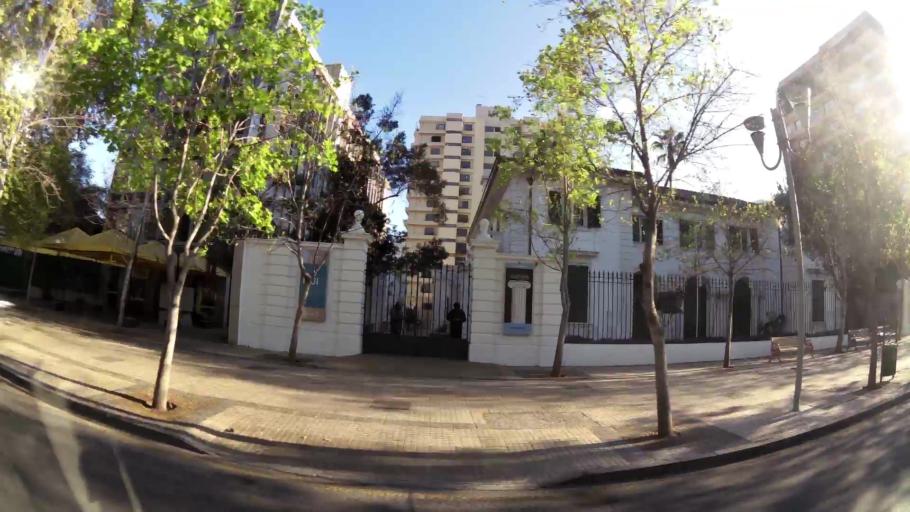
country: CL
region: Santiago Metropolitan
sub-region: Provincia de Santiago
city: Villa Presidente Frei, Nunoa, Santiago, Chile
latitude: -33.4144
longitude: -70.5956
